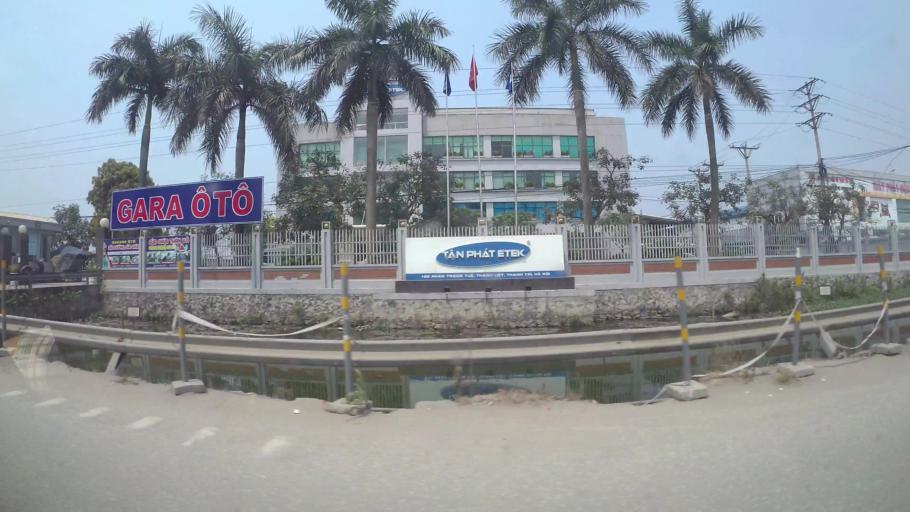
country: VN
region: Ha Noi
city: Van Dien
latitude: 20.9523
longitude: 105.8169
